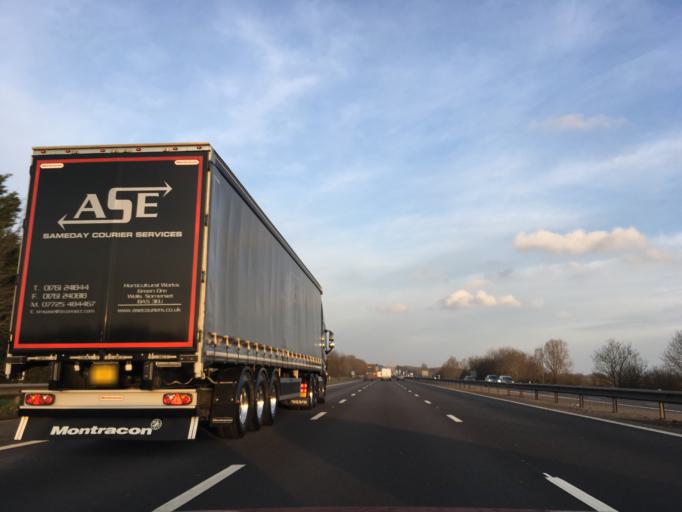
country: GB
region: England
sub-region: Worcestershire
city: Bredon
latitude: 52.0362
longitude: -2.1287
